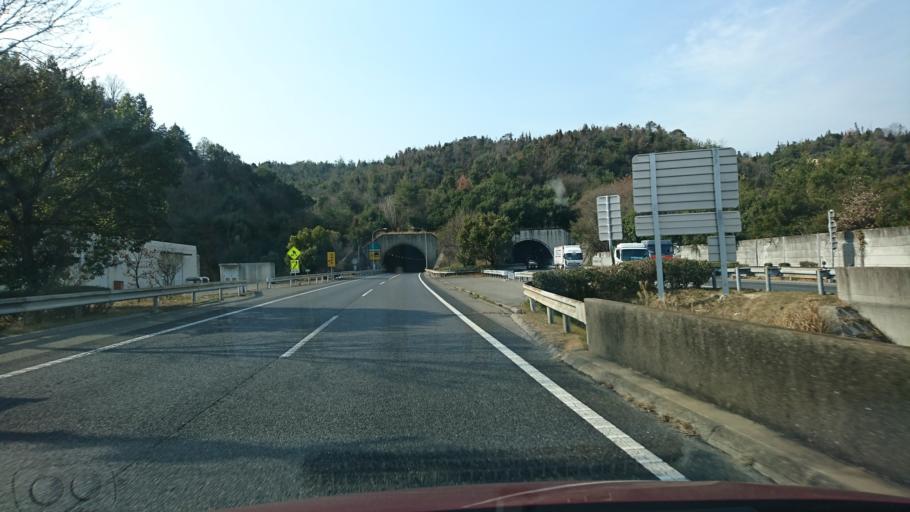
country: JP
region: Hiroshima
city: Fukuyama
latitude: 34.4813
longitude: 133.3081
